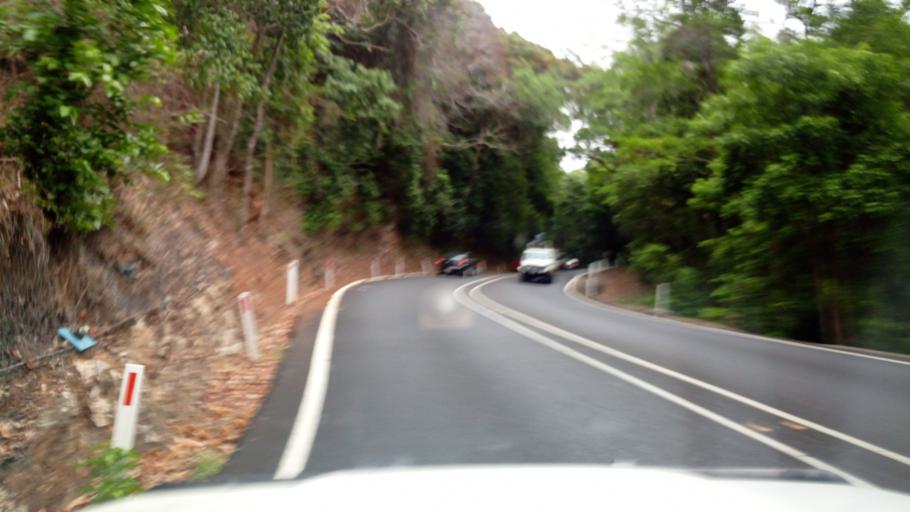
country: AU
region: Queensland
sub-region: Tablelands
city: Kuranda
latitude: -16.8439
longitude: 145.6731
